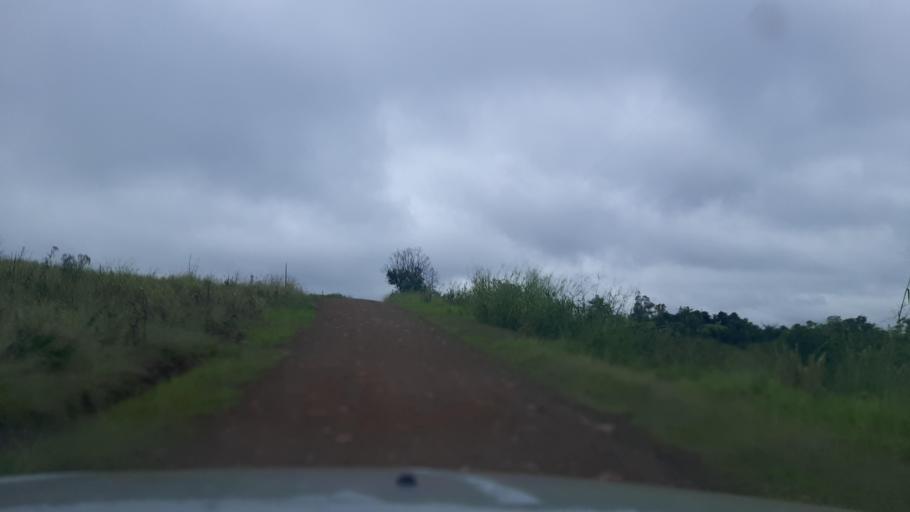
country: BR
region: Parana
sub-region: Ampere
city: Ampere
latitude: -26.0566
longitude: -53.5528
